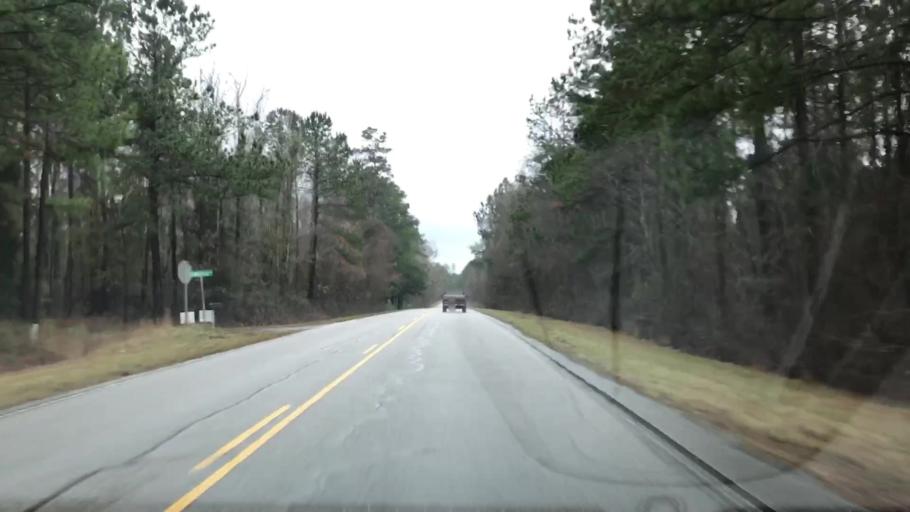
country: US
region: South Carolina
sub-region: Williamsburg County
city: Andrews
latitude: 33.5252
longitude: -79.4904
